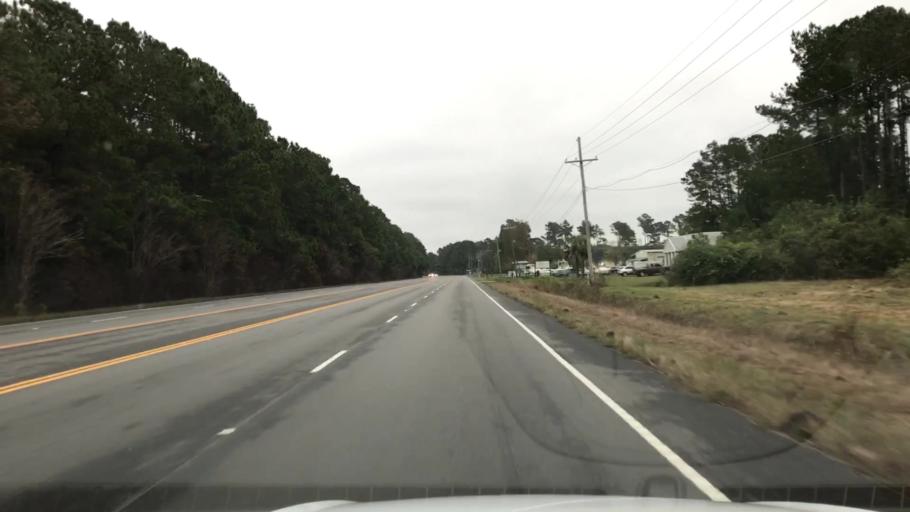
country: US
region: South Carolina
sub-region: Charleston County
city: Awendaw
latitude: 33.0967
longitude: -79.4738
